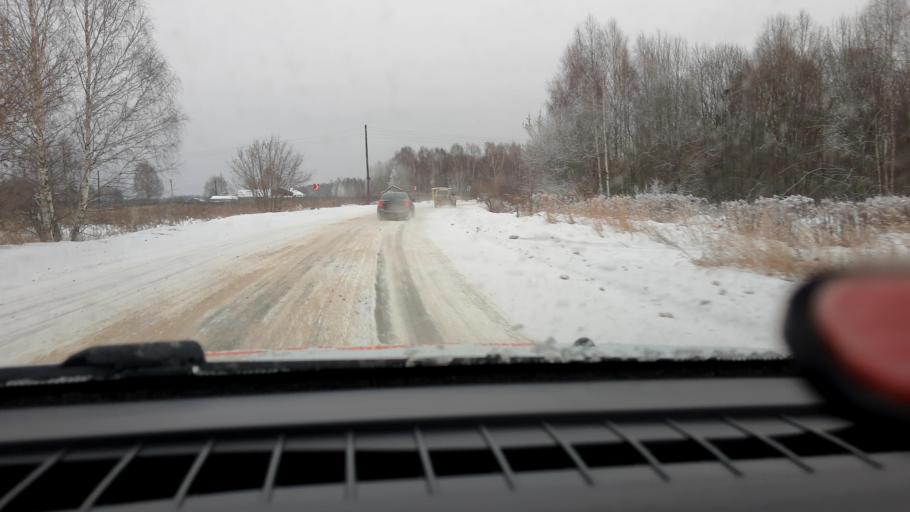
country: RU
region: Nizjnij Novgorod
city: Pamyat' Parizhskoy Kommuny
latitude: 56.2486
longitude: 44.4890
